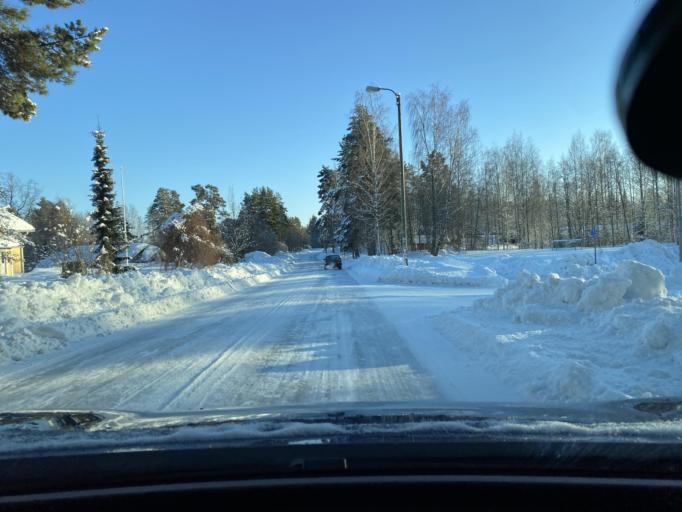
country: FI
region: Southern Savonia
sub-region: Mikkeli
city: Kangasniemi
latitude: 61.9993
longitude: 26.6280
